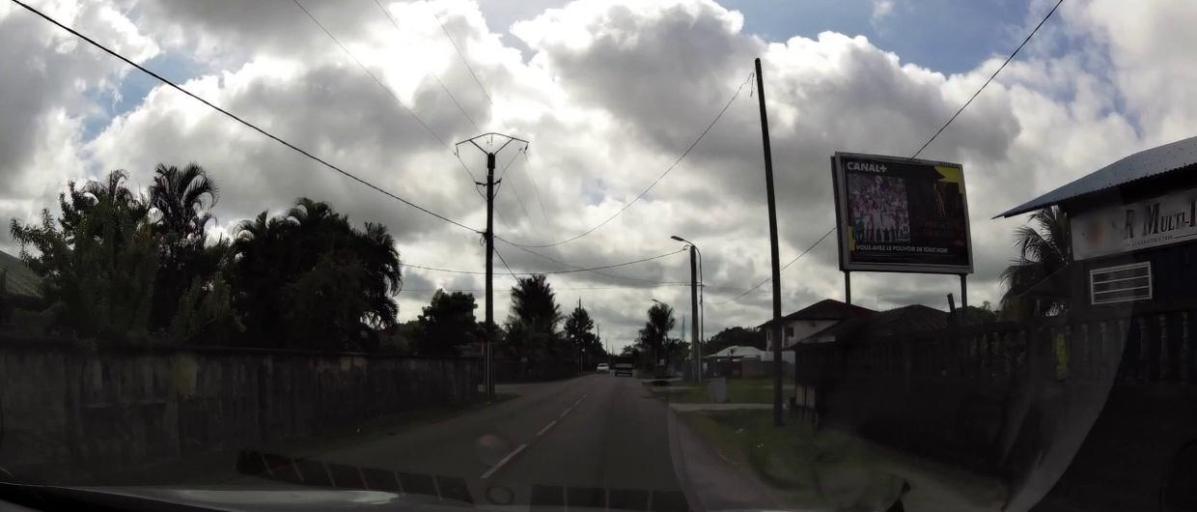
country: GF
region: Guyane
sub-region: Guyane
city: Matoury
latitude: 4.8755
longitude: -52.3349
